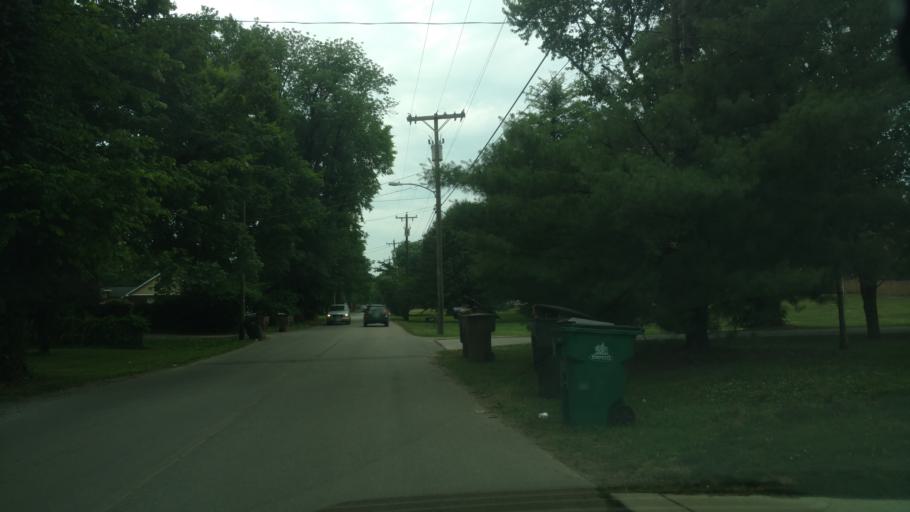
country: US
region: Tennessee
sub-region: Davidson County
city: Nashville
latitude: 36.1890
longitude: -86.7242
